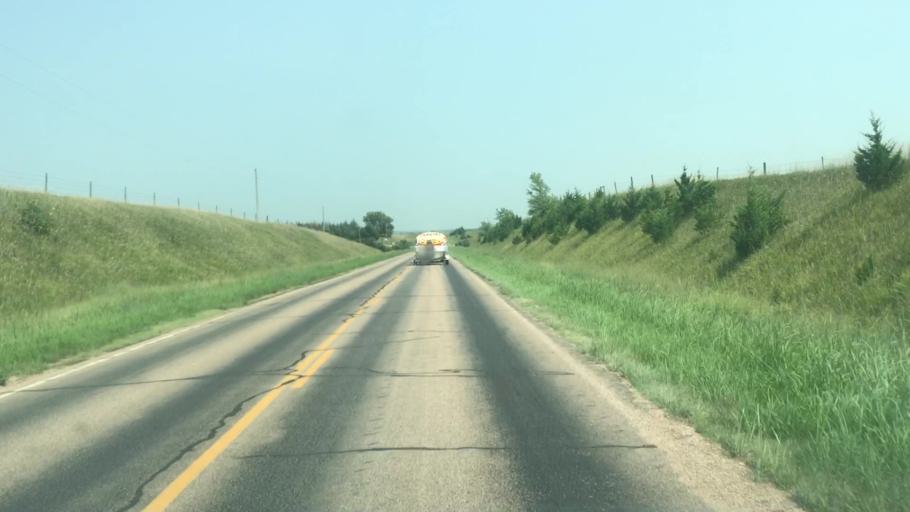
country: US
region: Nebraska
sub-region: Sherman County
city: Loup City
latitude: 41.2791
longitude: -98.9043
